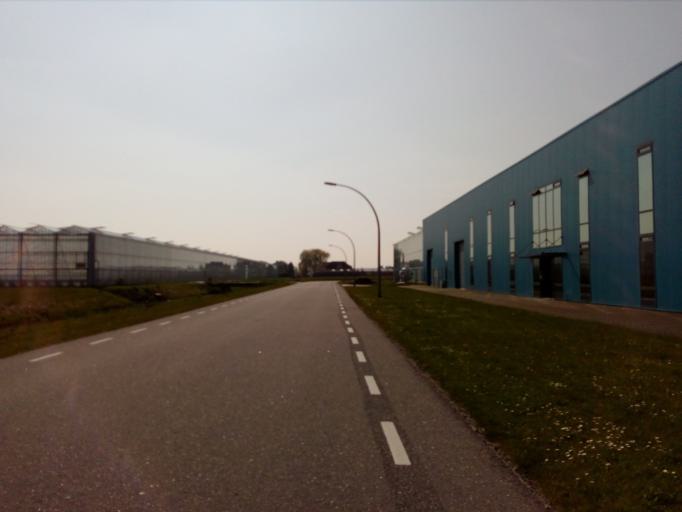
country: NL
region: South Holland
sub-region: Gemeente Lansingerland
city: Bleiswijk
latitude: 52.0305
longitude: 4.5312
